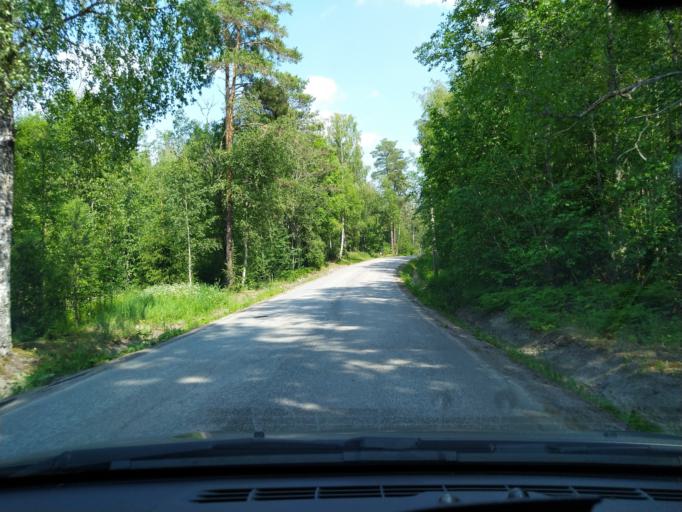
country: FI
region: Uusimaa
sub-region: Helsinki
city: Saukkola
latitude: 60.3635
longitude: 24.1010
